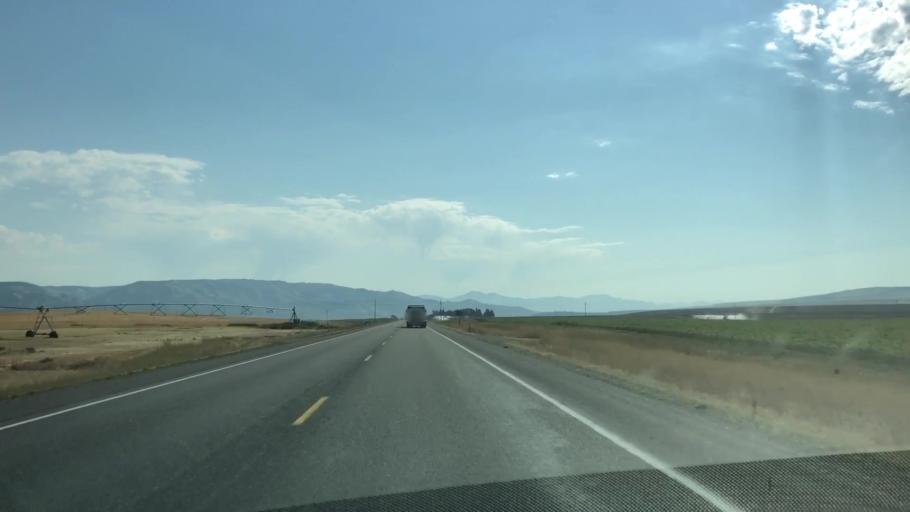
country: US
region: Idaho
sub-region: Jefferson County
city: Rigby
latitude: 43.6134
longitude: -111.7529
